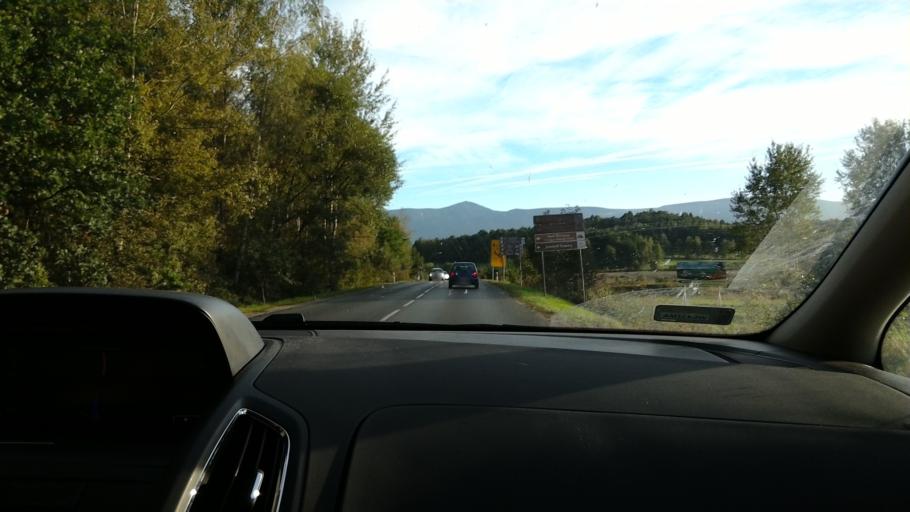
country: PL
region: Lower Silesian Voivodeship
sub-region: Powiat jeleniogorski
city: Myslakowice
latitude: 50.8618
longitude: 15.7742
